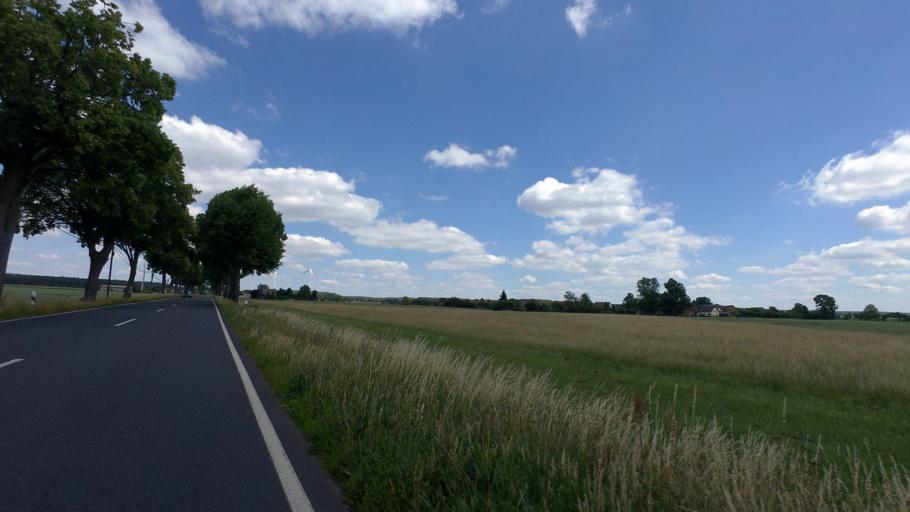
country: DE
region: Brandenburg
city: Sonnewalde
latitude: 51.7074
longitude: 13.6655
